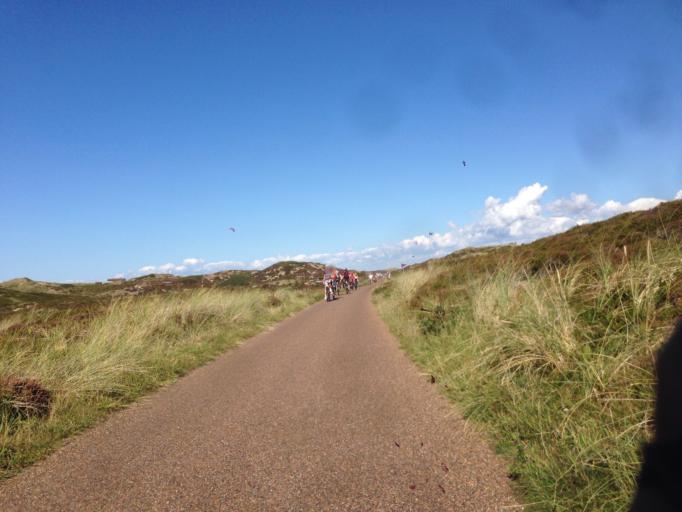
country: DE
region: Schleswig-Holstein
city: List
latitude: 54.9885
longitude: 8.3563
